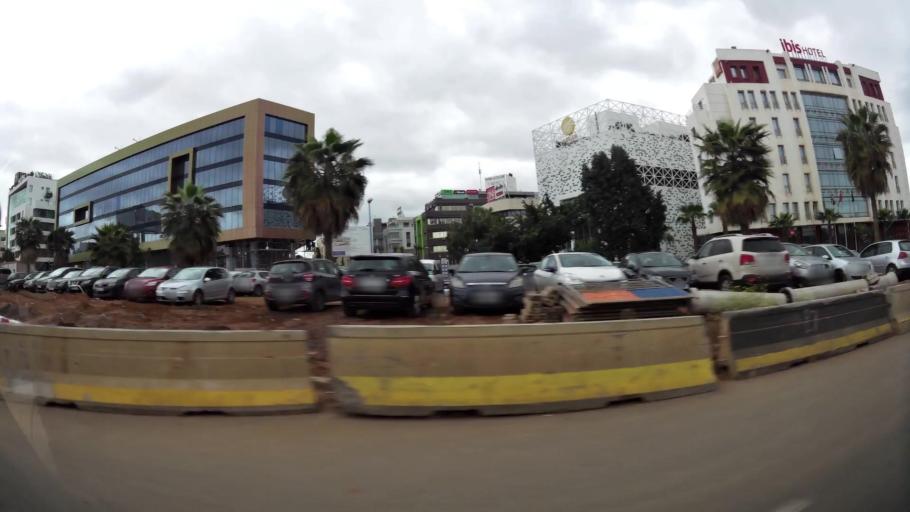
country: MA
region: Grand Casablanca
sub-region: Casablanca
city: Casablanca
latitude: 33.5386
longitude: -7.6401
